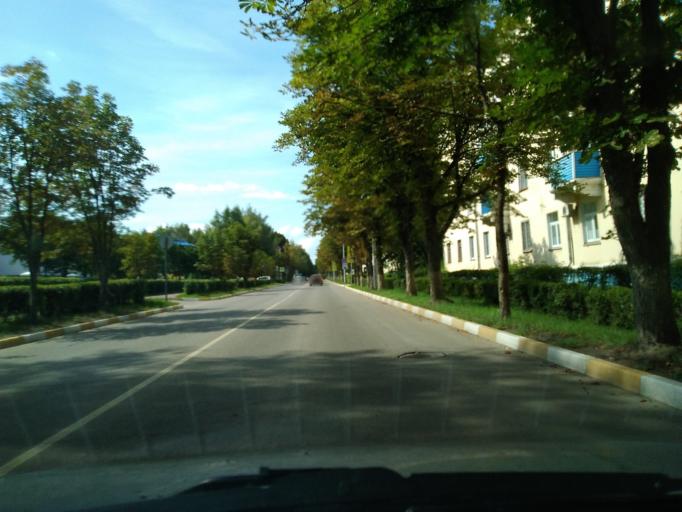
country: RU
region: Moskovskaya
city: Voskresensk
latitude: 55.3242
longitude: 38.6695
